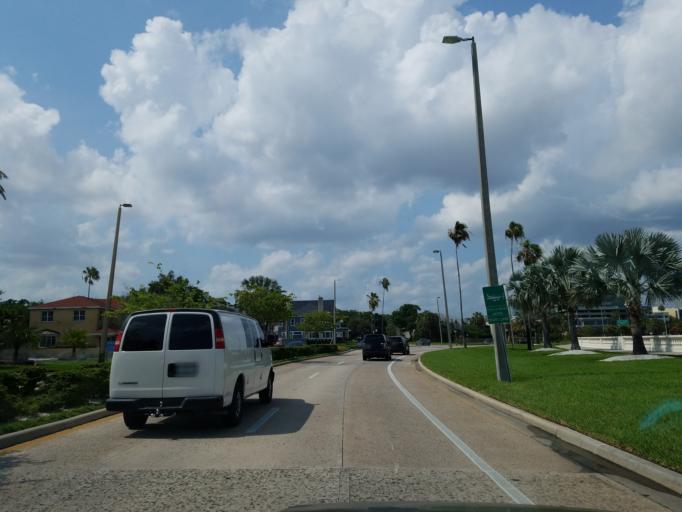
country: US
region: Florida
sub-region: Hillsborough County
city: Tampa
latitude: 27.9349
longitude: -82.4672
